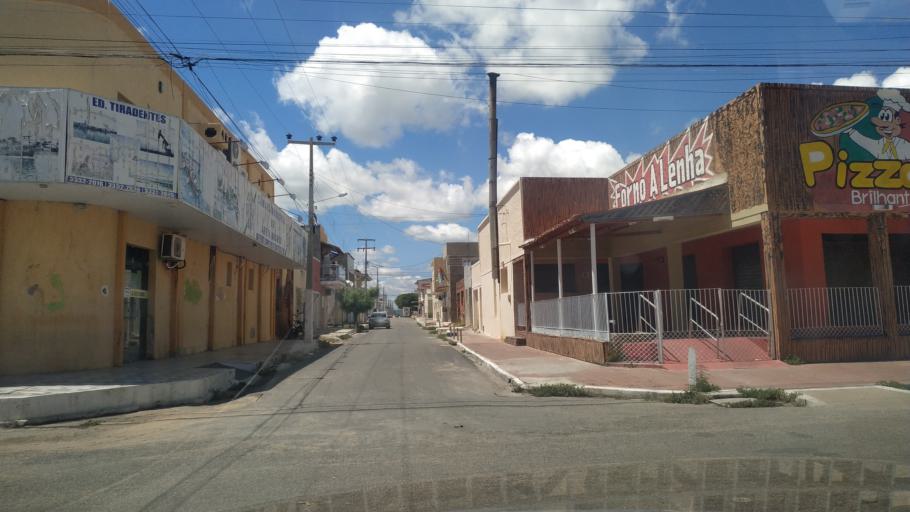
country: BR
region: Rio Grande do Norte
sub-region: Areia Branca
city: Areia Branca
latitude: -4.9548
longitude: -37.1356
